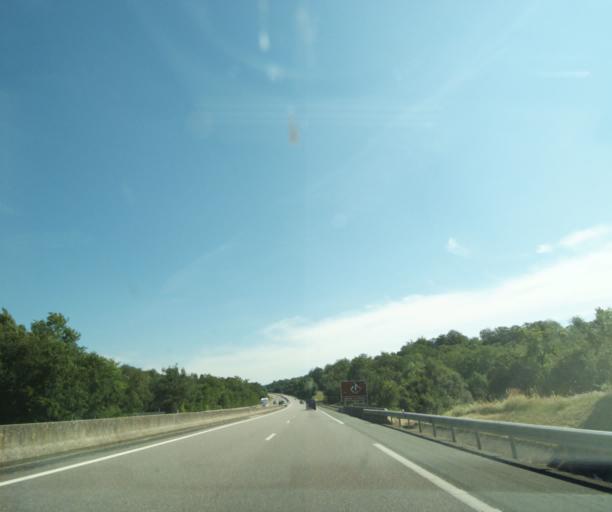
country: FR
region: Lorraine
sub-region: Departement de Meurthe-et-Moselle
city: Colombey-les-Belles
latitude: 48.4840
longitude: 5.8986
